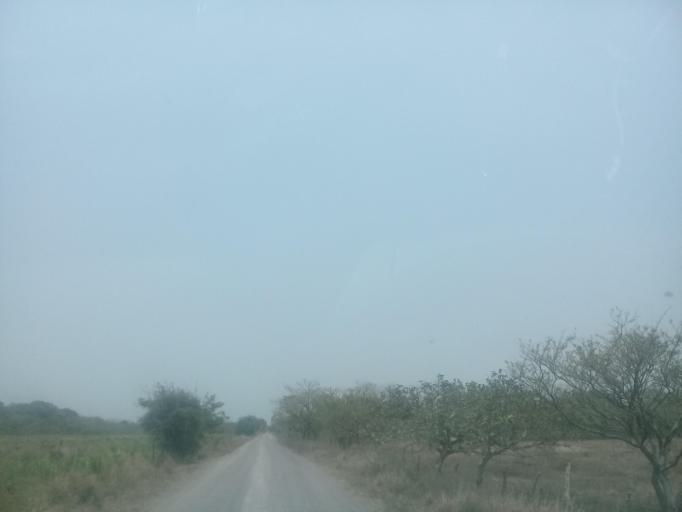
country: MX
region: Veracruz
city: Jamapa
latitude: 19.0807
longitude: -96.2391
